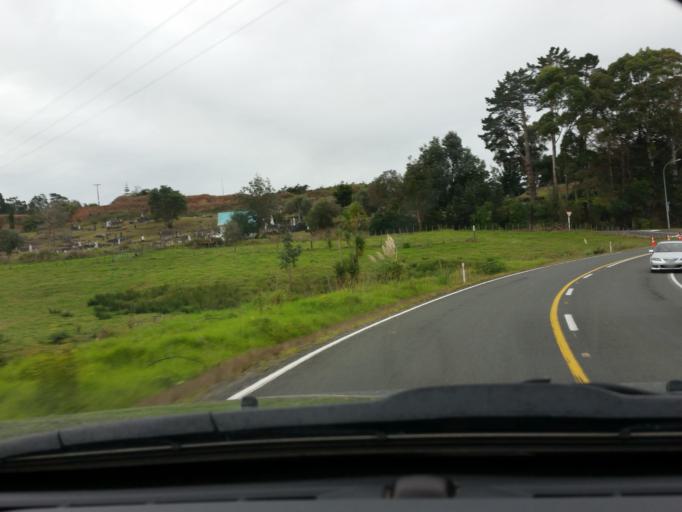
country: NZ
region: Northland
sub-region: Kaipara District
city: Dargaville
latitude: -35.9616
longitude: 173.8686
